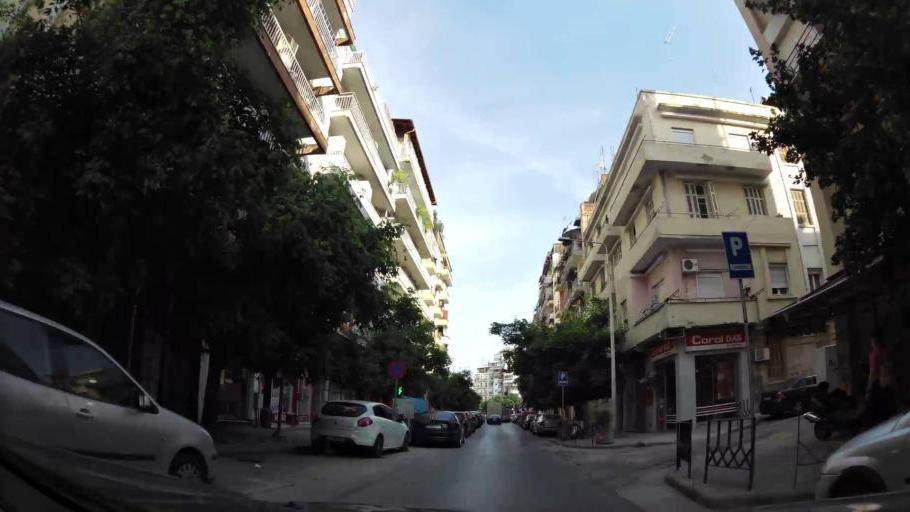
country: GR
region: Central Macedonia
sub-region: Nomos Thessalonikis
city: Sykies
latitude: 40.6421
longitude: 22.9428
